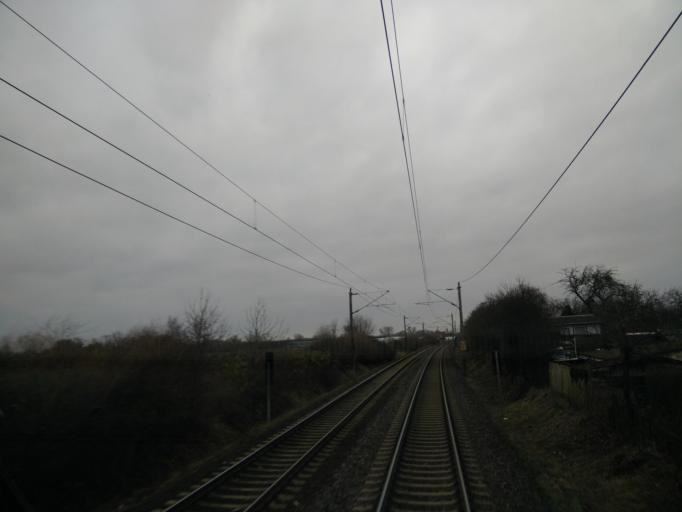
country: DE
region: Mecklenburg-Vorpommern
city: Lewenberg
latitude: 53.6550
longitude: 11.4007
